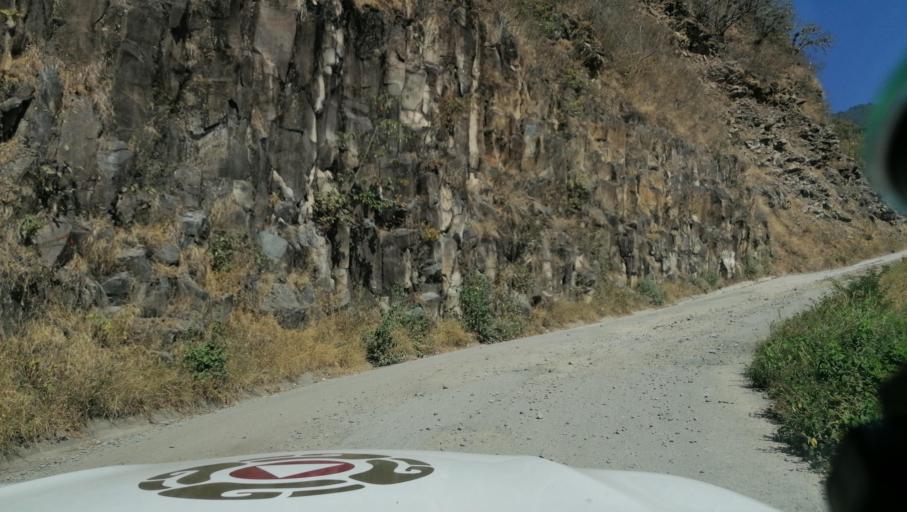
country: GT
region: San Marcos
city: Tacana
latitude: 15.1906
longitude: -92.1861
